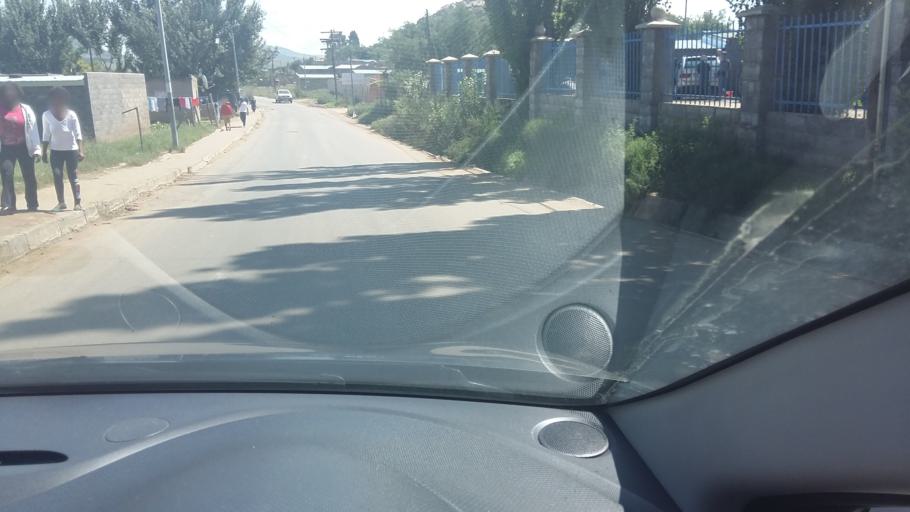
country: LS
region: Maseru
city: Maseru
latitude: -29.3367
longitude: 27.4568
